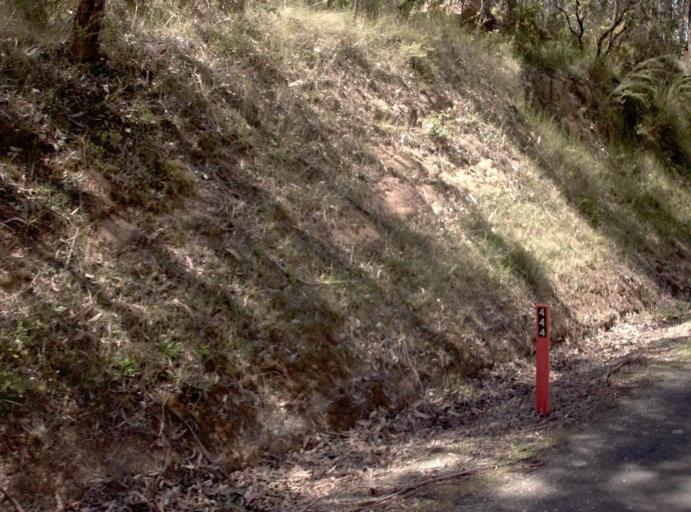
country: AU
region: New South Wales
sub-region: Bombala
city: Bombala
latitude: -37.5658
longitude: 149.0774
